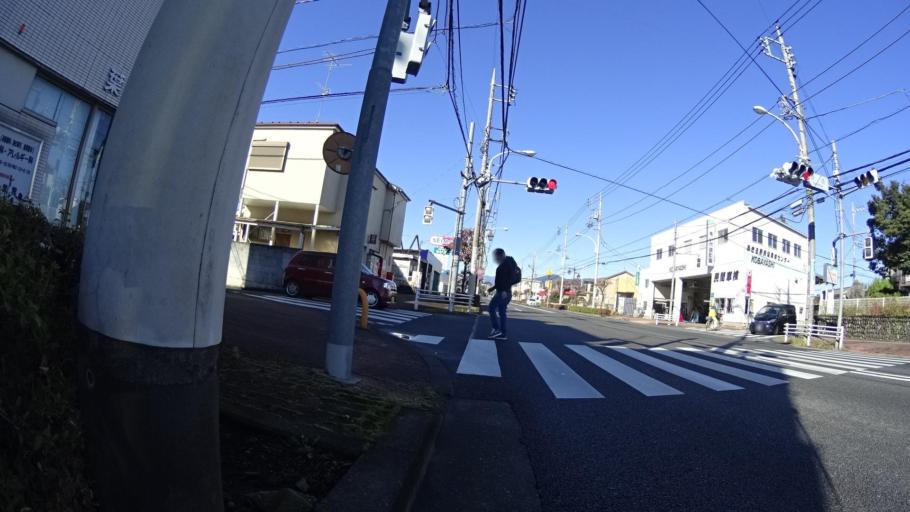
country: JP
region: Tokyo
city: Itsukaichi
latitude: 35.7252
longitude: 139.2697
